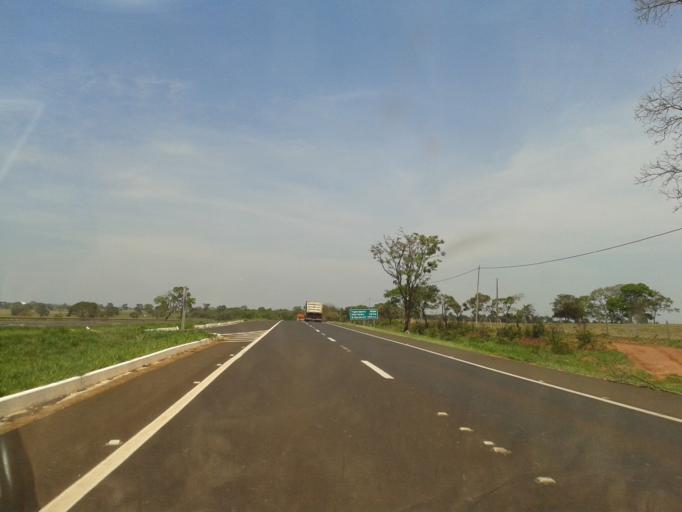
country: BR
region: Minas Gerais
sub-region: Monte Alegre De Minas
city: Monte Alegre de Minas
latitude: -18.8930
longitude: -48.6627
